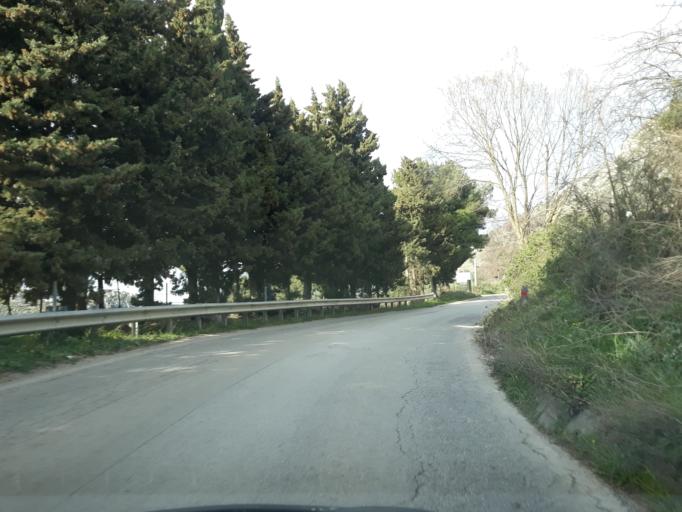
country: IT
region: Sicily
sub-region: Palermo
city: Torretta
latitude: 38.1062
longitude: 13.2341
